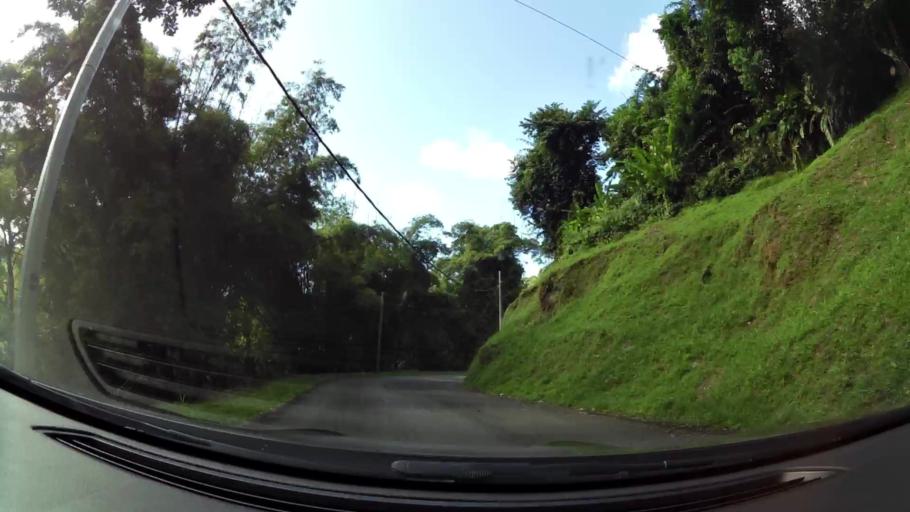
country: TT
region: Eastern Tobago
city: Roxborough
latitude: 11.3043
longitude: -60.6254
